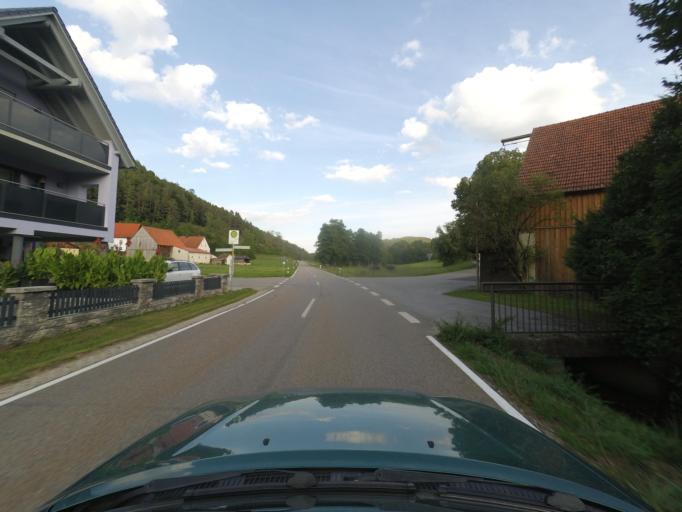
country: DE
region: Bavaria
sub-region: Upper Palatinate
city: Hirschbach
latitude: 49.5670
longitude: 11.5649
